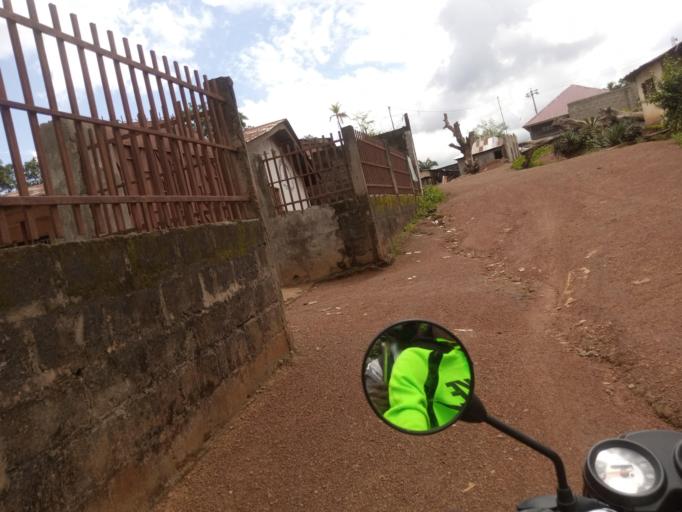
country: SL
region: Northern Province
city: Port Loko
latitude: 8.7630
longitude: -12.7847
